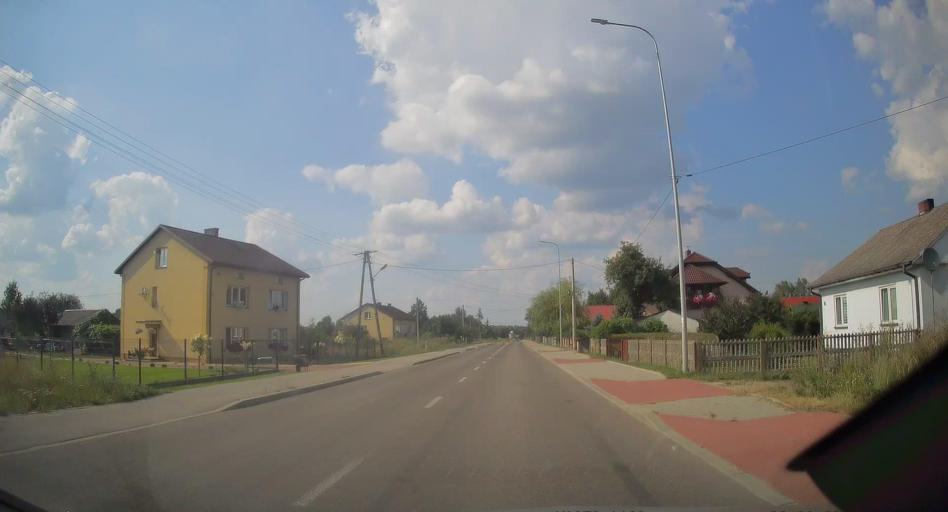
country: PL
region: Swietokrzyskie
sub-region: Powiat konecki
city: Radoszyce
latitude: 51.0514
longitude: 20.2812
